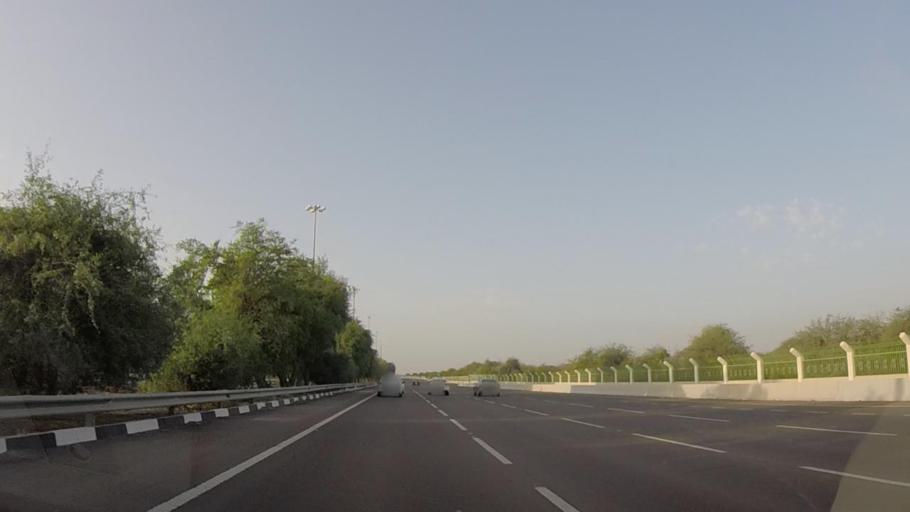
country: AE
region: Dubai
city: Dubai
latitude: 24.8570
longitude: 54.9030
